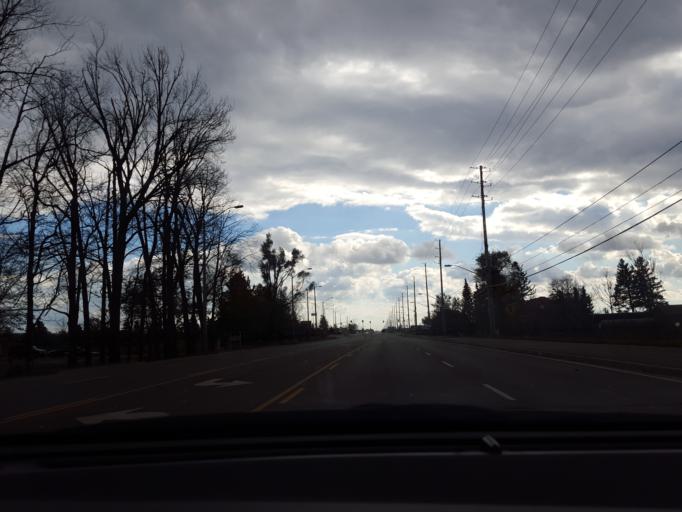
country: CA
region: Ontario
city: Brampton
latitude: 43.6398
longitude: -79.7930
